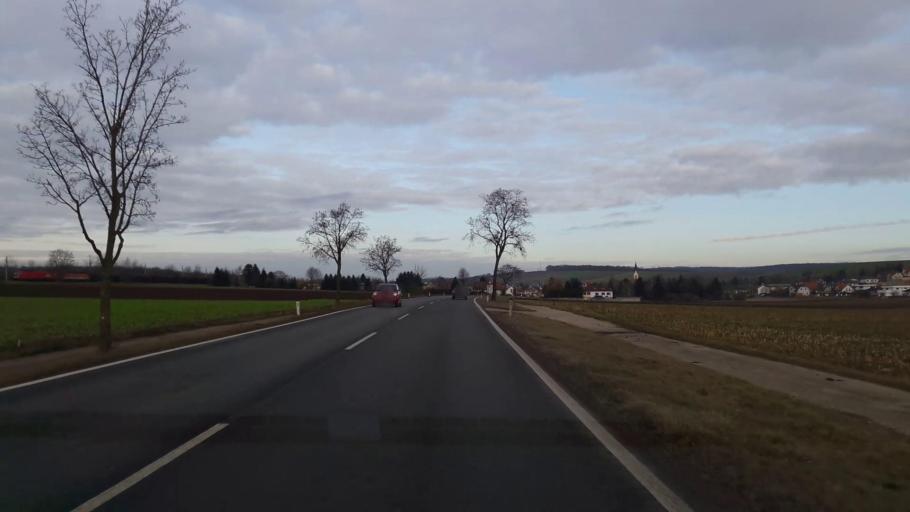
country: AT
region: Lower Austria
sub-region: Politischer Bezirk Mistelbach
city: Mistelbach
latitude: 48.5997
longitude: 16.5428
